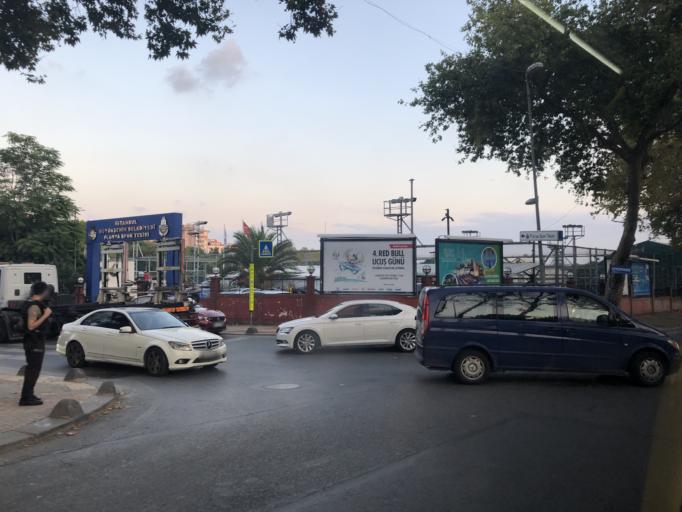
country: TR
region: Istanbul
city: Bahcelievler
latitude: 40.9759
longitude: 28.7909
